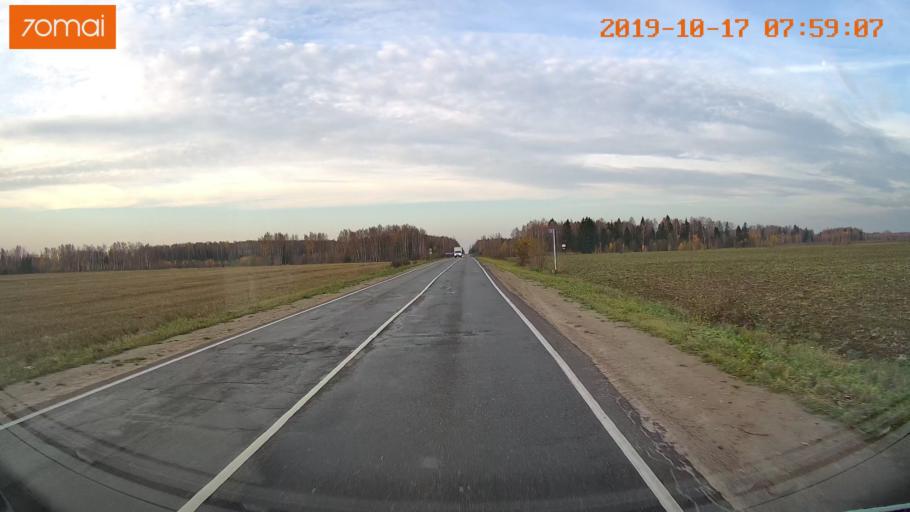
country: RU
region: Vladimir
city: Bavleny
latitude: 56.3964
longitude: 39.5446
